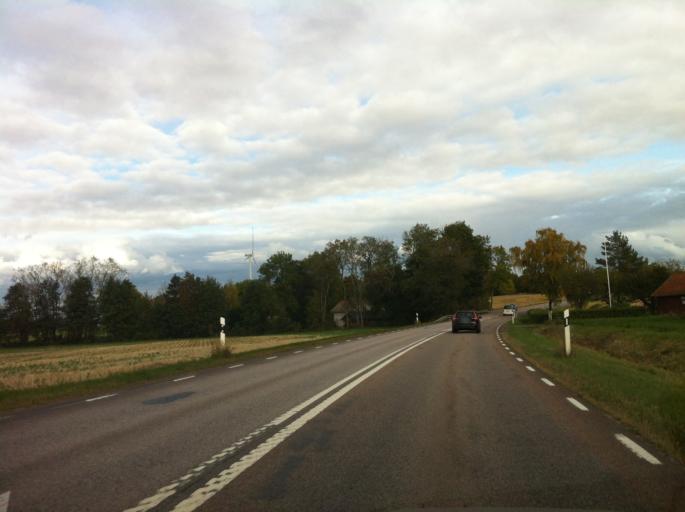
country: SE
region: OEstergoetland
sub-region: Vadstena Kommun
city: Vadstena
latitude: 58.4756
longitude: 14.9522
